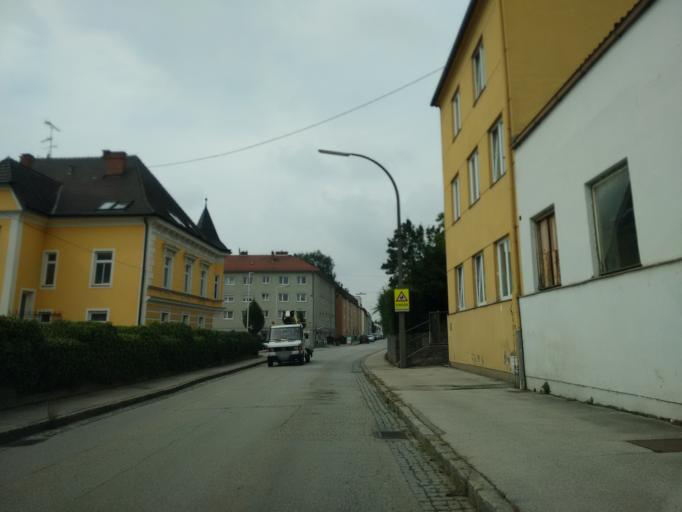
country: AT
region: Upper Austria
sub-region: Politischer Bezirk Grieskirchen
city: Grieskirchen
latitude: 48.2318
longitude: 13.8401
